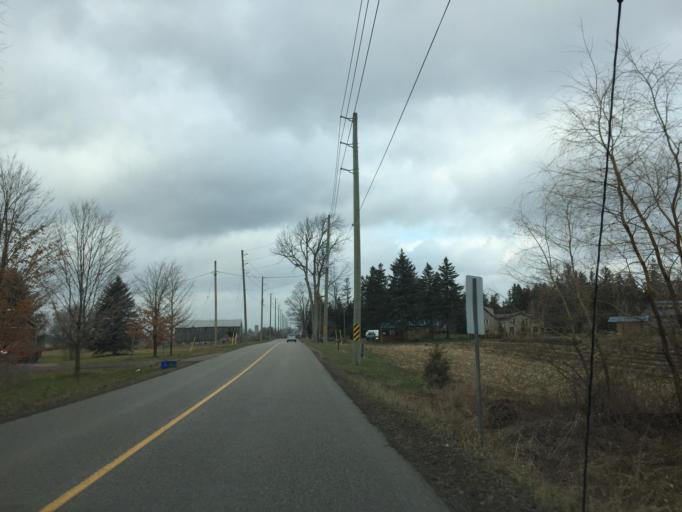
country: CA
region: Ontario
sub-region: Wellington County
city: Guelph
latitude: 43.4899
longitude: -80.3417
